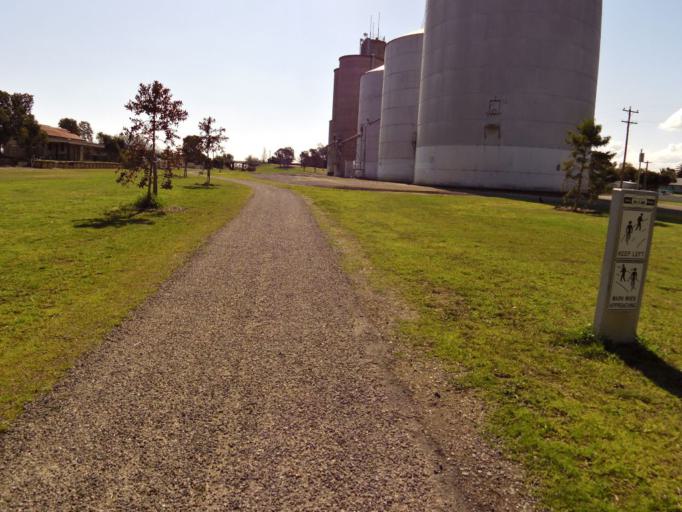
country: AU
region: New South Wales
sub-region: Corowa Shire
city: Corowa
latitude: -36.0549
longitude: 146.4635
